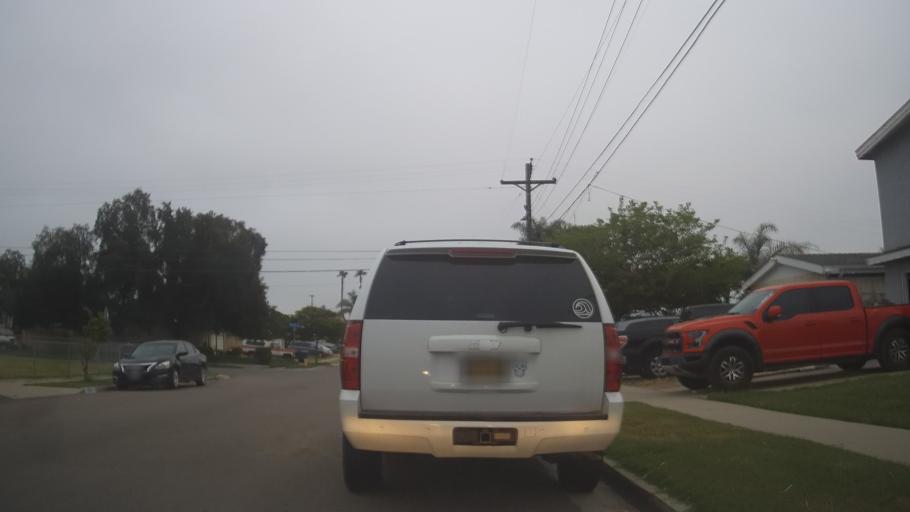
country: US
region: California
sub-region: San Diego County
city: Bonita
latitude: 32.6223
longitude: -117.0441
